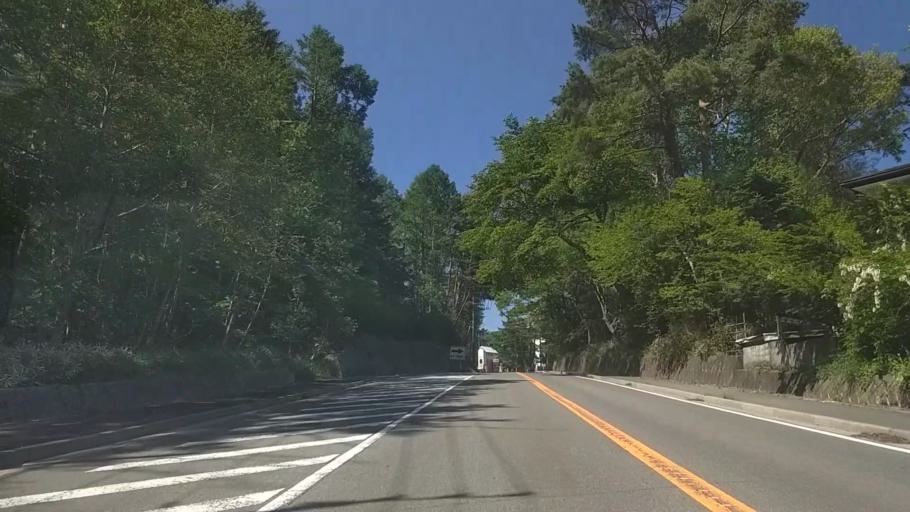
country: JP
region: Yamanashi
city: Nirasaki
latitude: 35.9040
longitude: 138.4434
